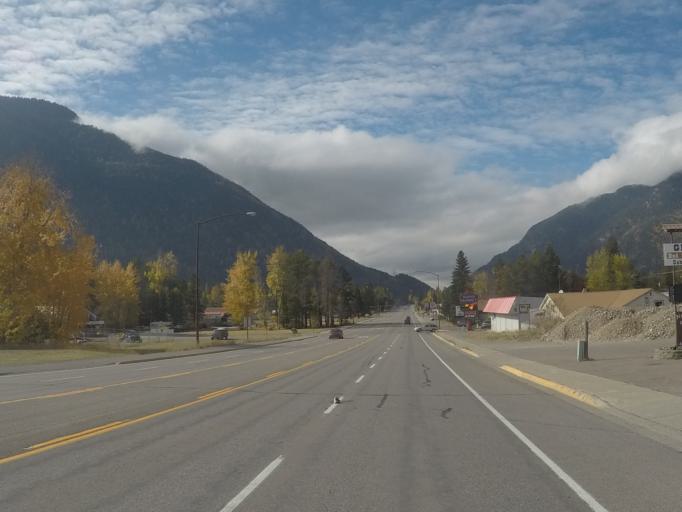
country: US
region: Montana
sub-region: Flathead County
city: Columbia Falls
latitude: 48.3858
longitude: -114.0564
